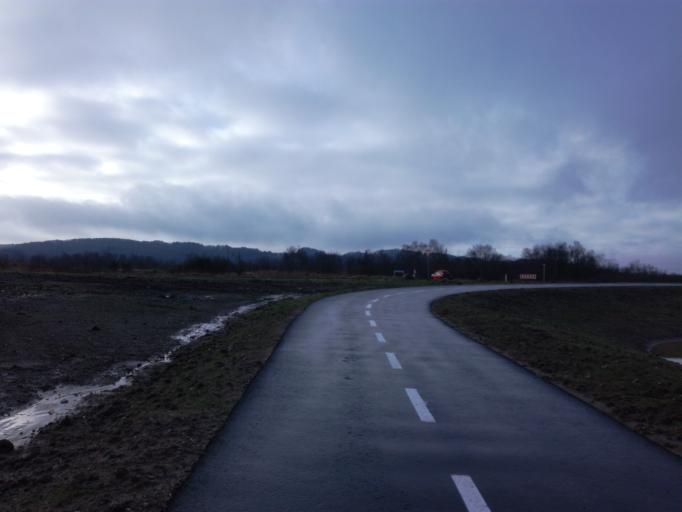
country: DK
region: South Denmark
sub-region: Vejle Kommune
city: Vejle
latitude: 55.7101
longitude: 9.4974
